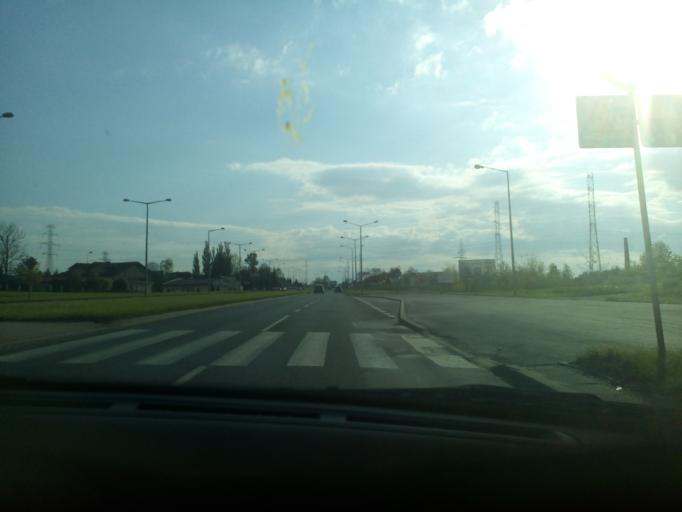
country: PL
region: Lesser Poland Voivodeship
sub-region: Powiat nowosadecki
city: Nawojowa
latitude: 49.5911
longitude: 20.7302
